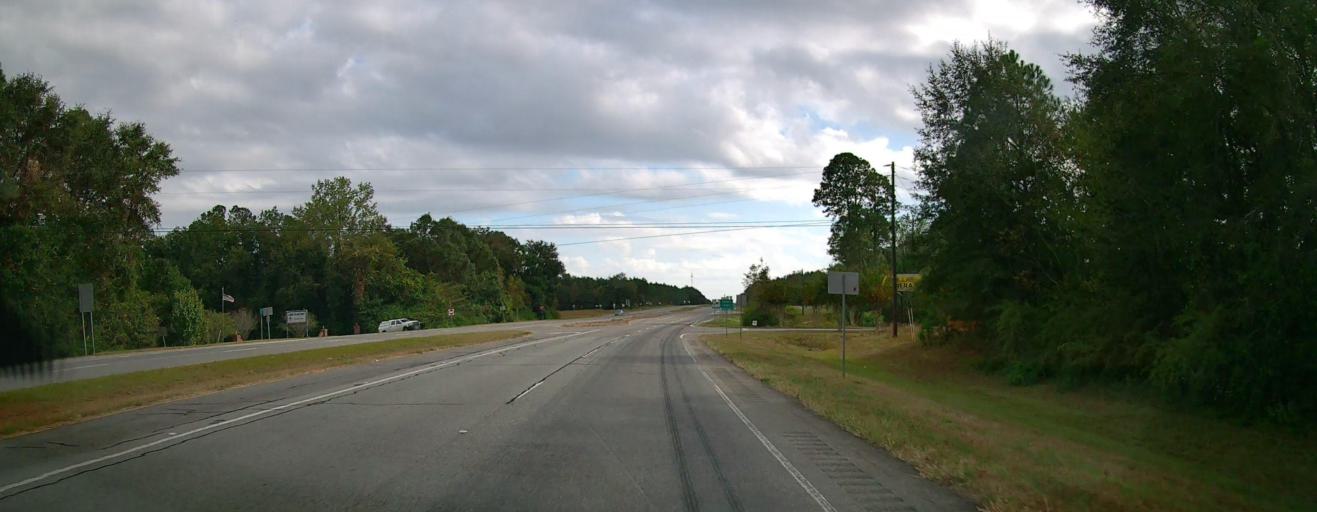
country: US
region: Georgia
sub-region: Thomas County
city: Meigs
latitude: 31.0784
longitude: -84.0811
